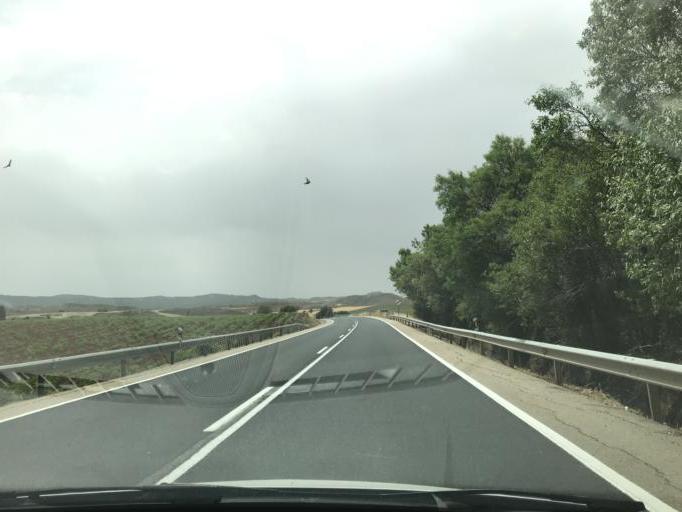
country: ES
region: Castille-La Mancha
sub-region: Provincia de Cuenca
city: Villar de Domingo Garcia
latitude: 40.2514
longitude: -2.3093
